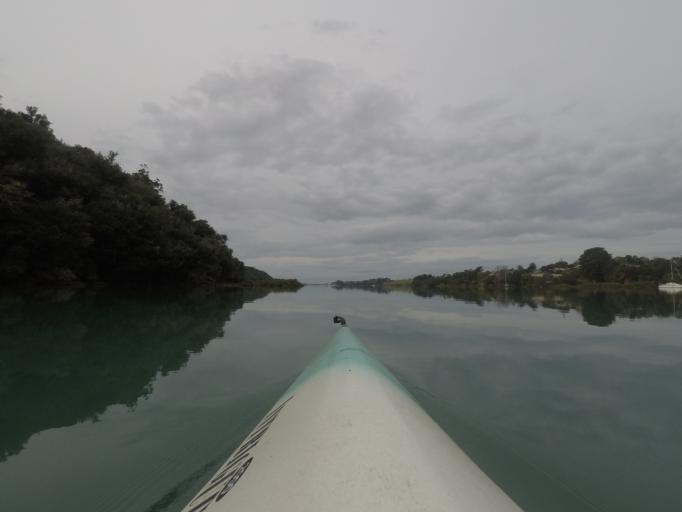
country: NZ
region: Auckland
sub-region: Auckland
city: Rothesay Bay
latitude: -36.6741
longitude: 174.7138
